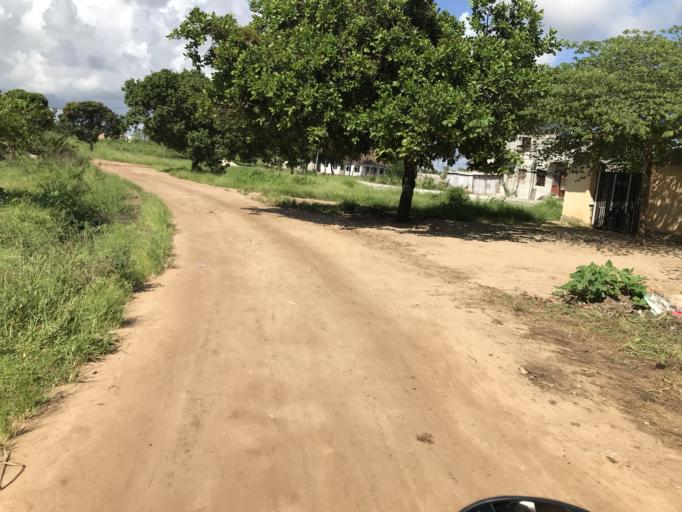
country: TZ
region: Dar es Salaam
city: Dar es Salaam
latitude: -6.8891
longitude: 39.4324
